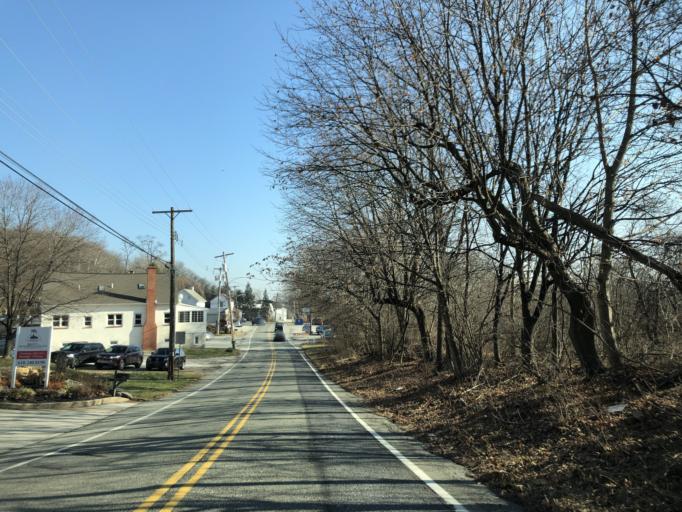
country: US
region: Pennsylvania
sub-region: Chester County
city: Malvern
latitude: 40.0728
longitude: -75.5251
